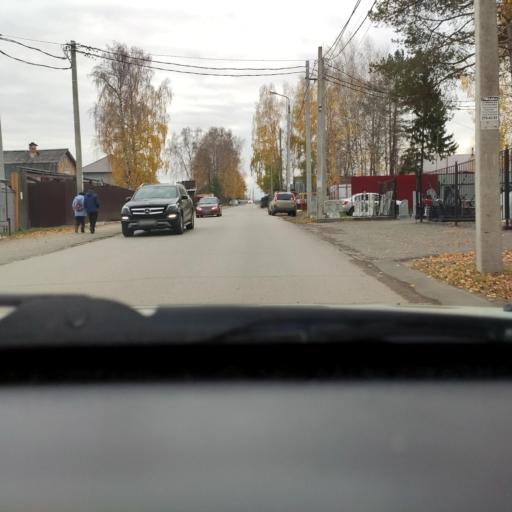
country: RU
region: Perm
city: Kondratovo
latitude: 58.0600
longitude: 56.1243
